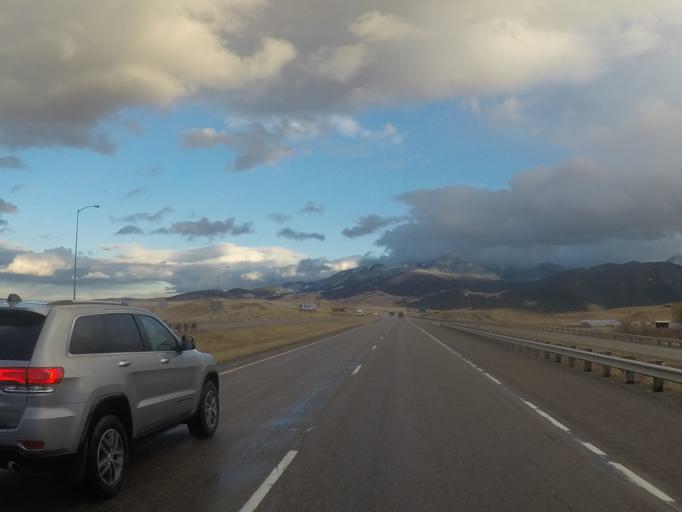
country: US
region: Montana
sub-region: Park County
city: Livingston
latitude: 45.6508
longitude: -110.6112
